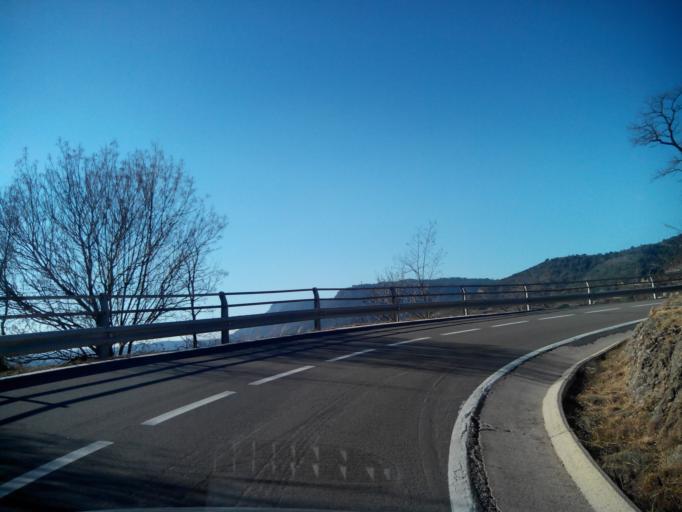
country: ES
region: Catalonia
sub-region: Provincia de Barcelona
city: Berga
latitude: 42.1056
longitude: 1.8431
